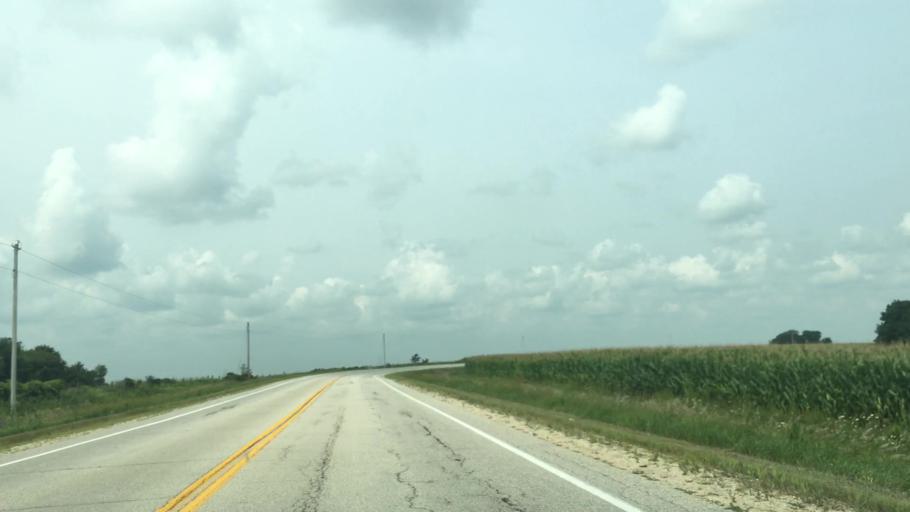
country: US
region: Minnesota
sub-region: Fillmore County
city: Harmony
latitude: 43.6668
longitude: -91.9343
